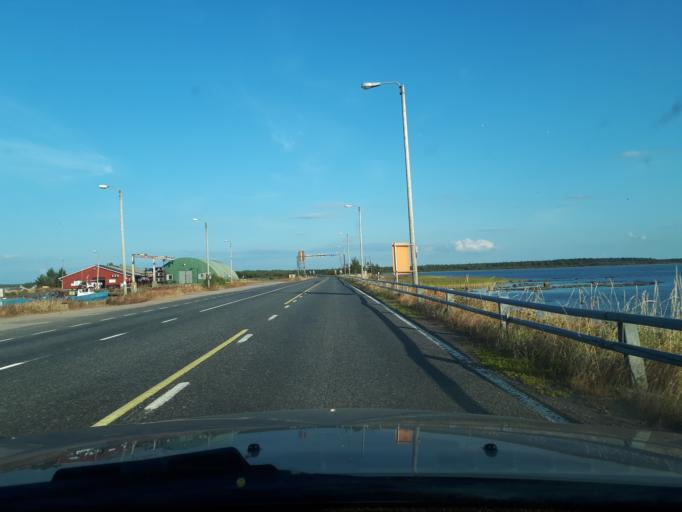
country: FI
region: Northern Ostrobothnia
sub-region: Oulu
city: Lumijoki
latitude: 65.0074
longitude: 25.2004
